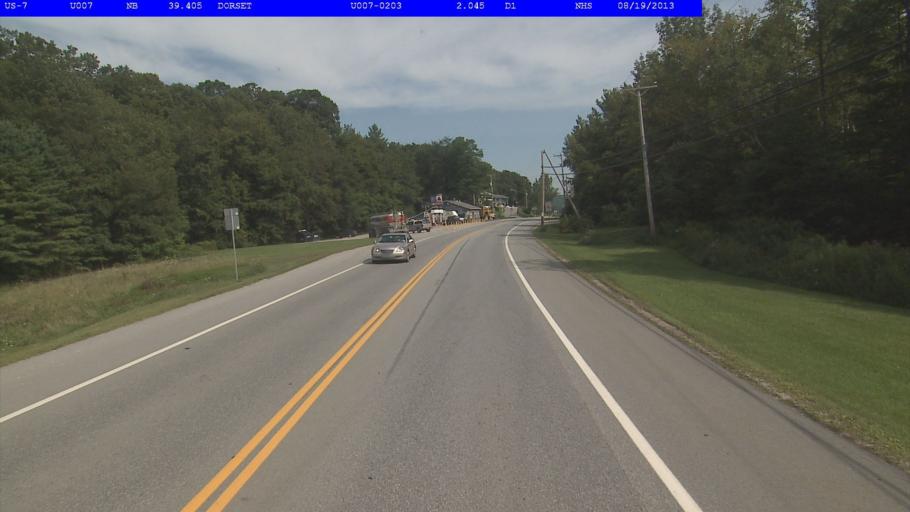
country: US
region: Vermont
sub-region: Bennington County
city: Manchester Center
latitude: 43.2386
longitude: -73.0106
